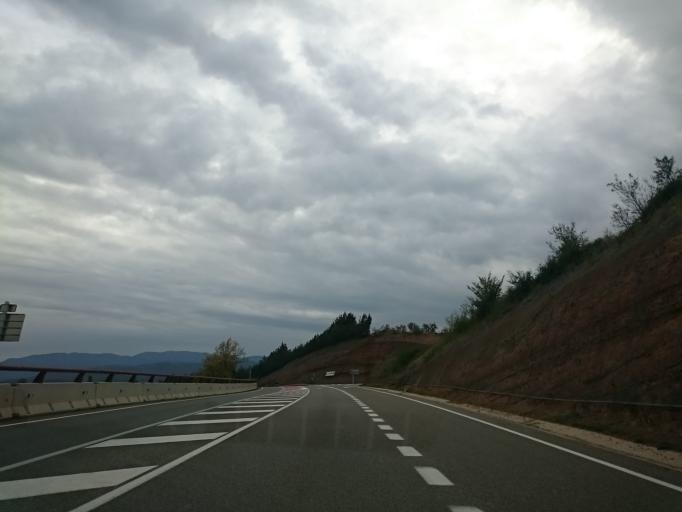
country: ES
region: Catalonia
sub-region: Provincia de Lleida
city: Tremp
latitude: 42.1818
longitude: 0.8982
